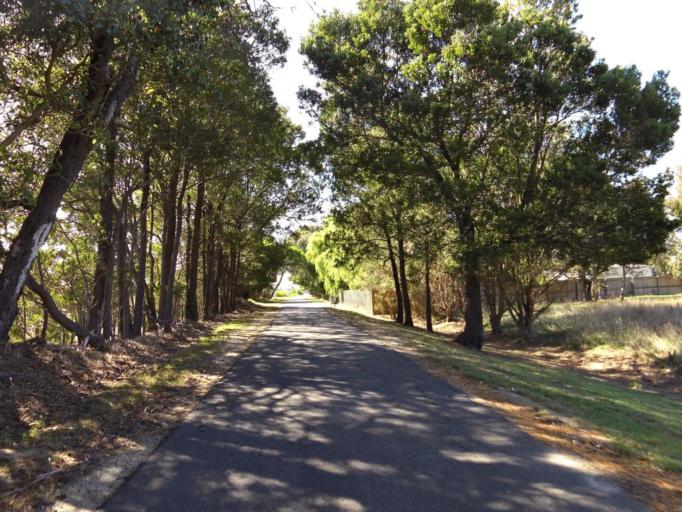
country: AU
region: Victoria
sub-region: Bass Coast
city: North Wonthaggi
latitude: -38.6048
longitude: 145.5832
